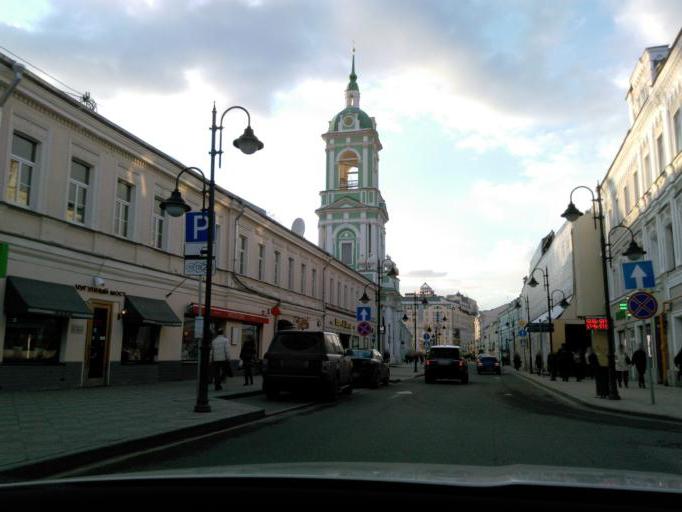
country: RU
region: Moscow
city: Zamoskvorech'ye
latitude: 55.7443
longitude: 37.6277
